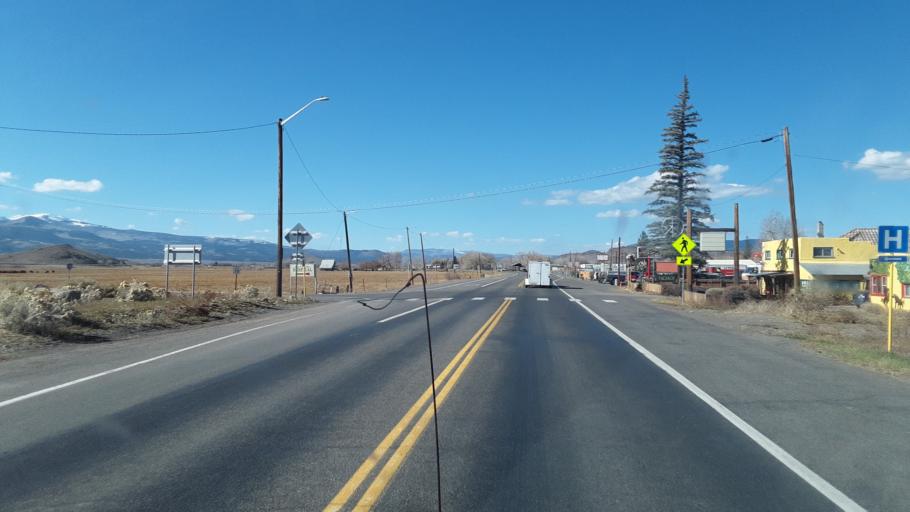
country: US
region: Colorado
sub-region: Rio Grande County
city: Del Norte
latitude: 37.6795
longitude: -106.3612
